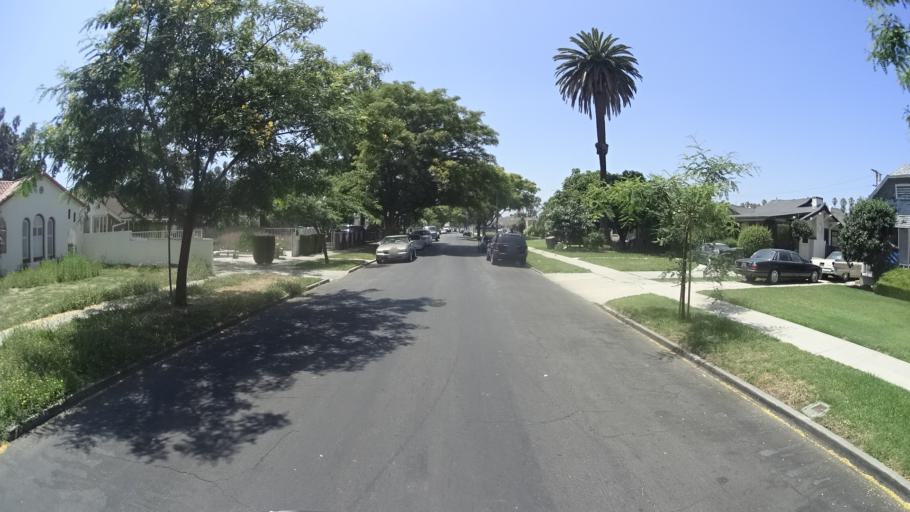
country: US
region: California
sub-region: Los Angeles County
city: View Park-Windsor Hills
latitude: 33.9988
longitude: -118.3214
